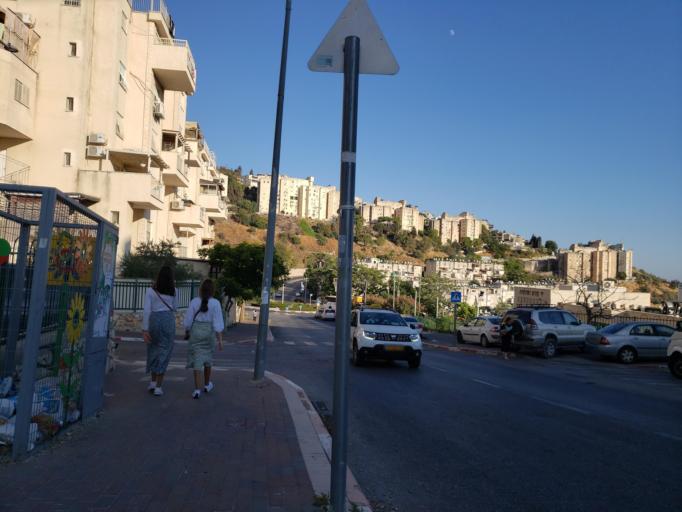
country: IL
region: Northern District
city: Safed
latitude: 32.9645
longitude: 35.4881
